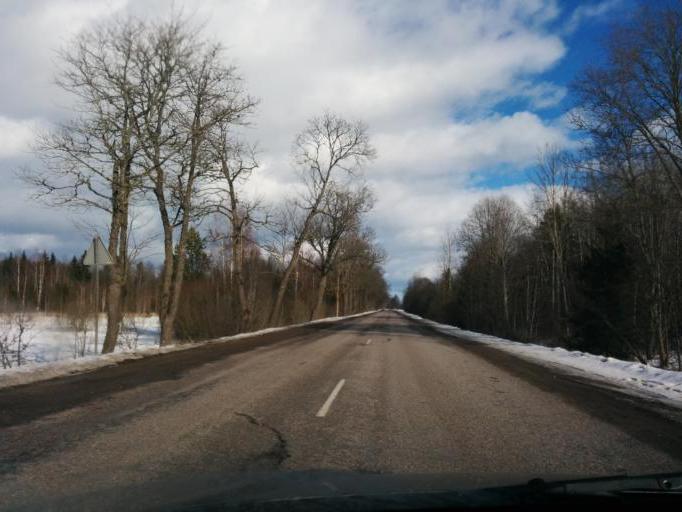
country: LV
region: Gulbenes Rajons
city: Gulbene
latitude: 57.1731
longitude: 26.8070
